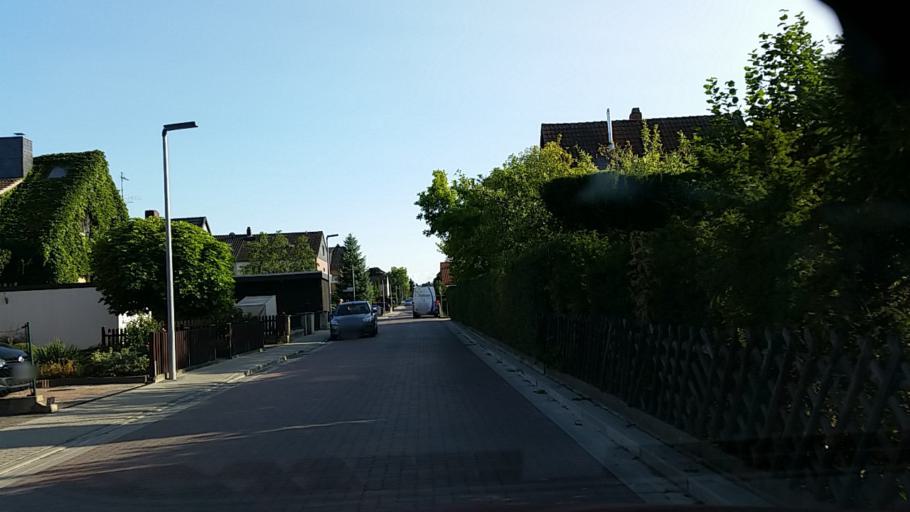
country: DE
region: Lower Saxony
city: Lehre
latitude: 52.3273
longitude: 10.6729
